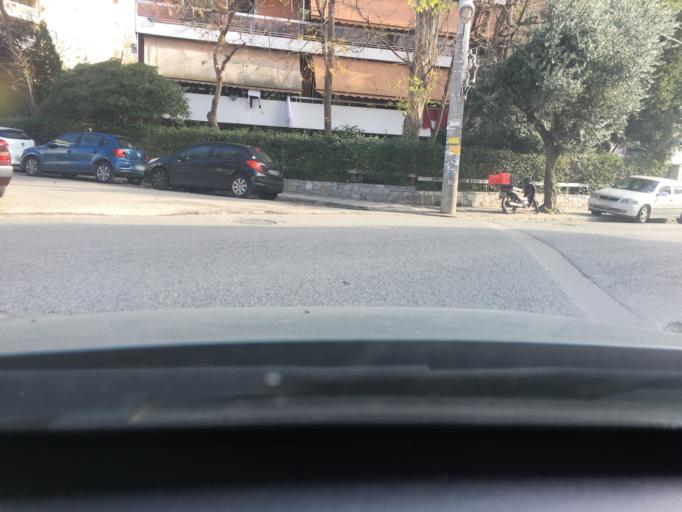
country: GR
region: Attica
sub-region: Nomarchia Athinas
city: Khalandrion
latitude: 38.0265
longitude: 23.7999
